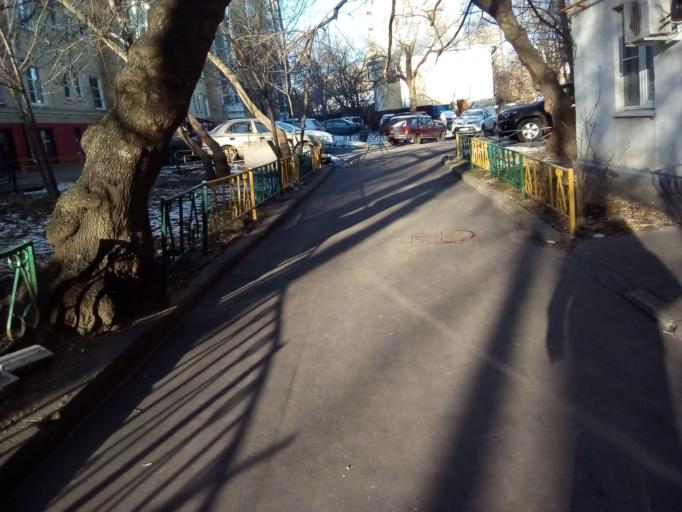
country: RU
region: Moskovskaya
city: Dorogomilovo
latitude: 55.7623
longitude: 37.5738
